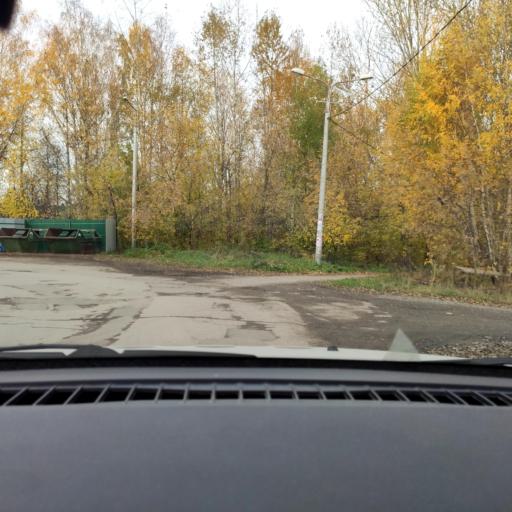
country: RU
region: Perm
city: Perm
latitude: 58.0643
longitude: 56.3483
